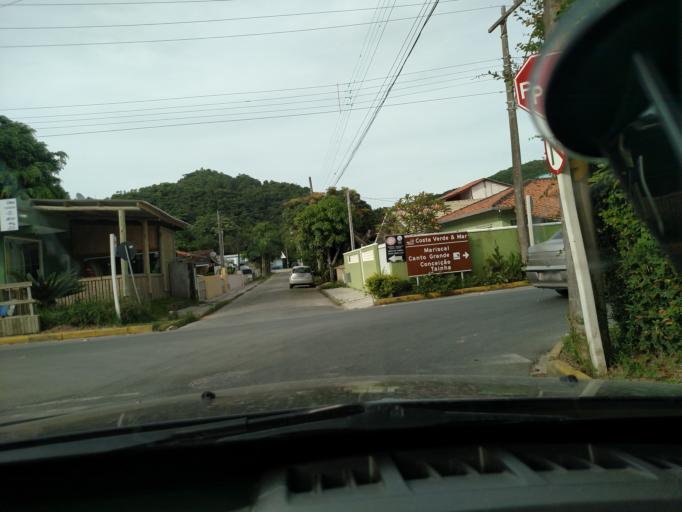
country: BR
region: Santa Catarina
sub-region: Porto Belo
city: Porto Belo
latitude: -27.1550
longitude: -48.4885
